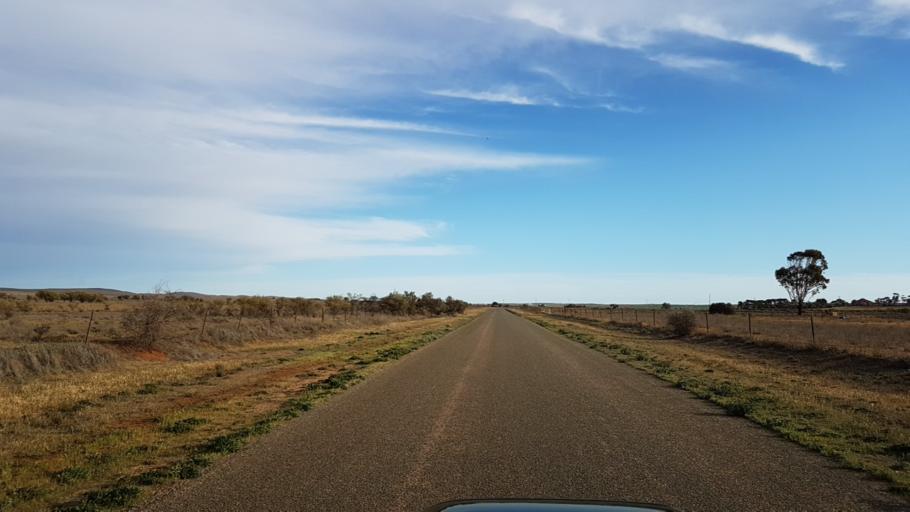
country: AU
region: South Australia
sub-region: Peterborough
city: Peterborough
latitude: -32.9863
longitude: 138.8503
